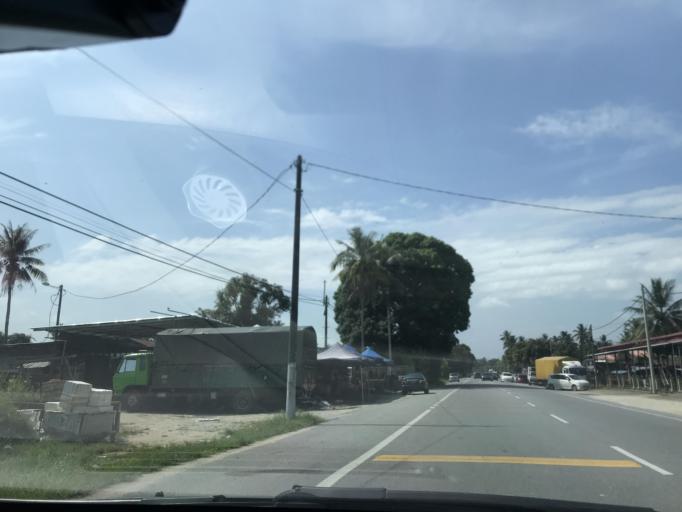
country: MY
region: Kelantan
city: Tumpat
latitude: 6.1439
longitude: 102.1658
